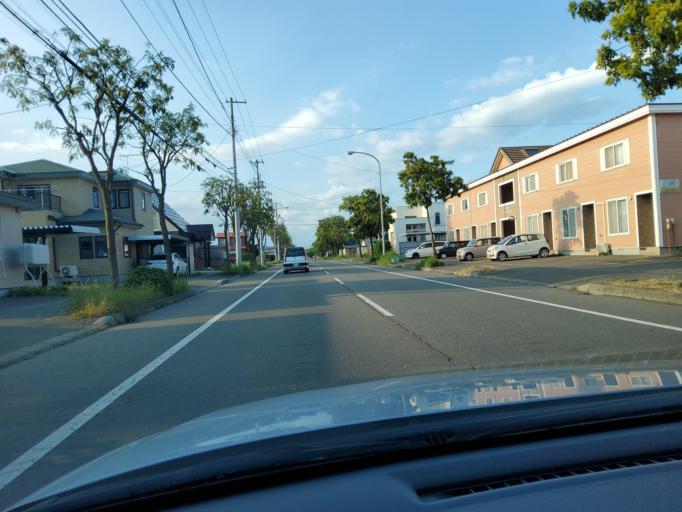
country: JP
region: Hokkaido
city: Obihiro
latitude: 42.9363
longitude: 143.1843
